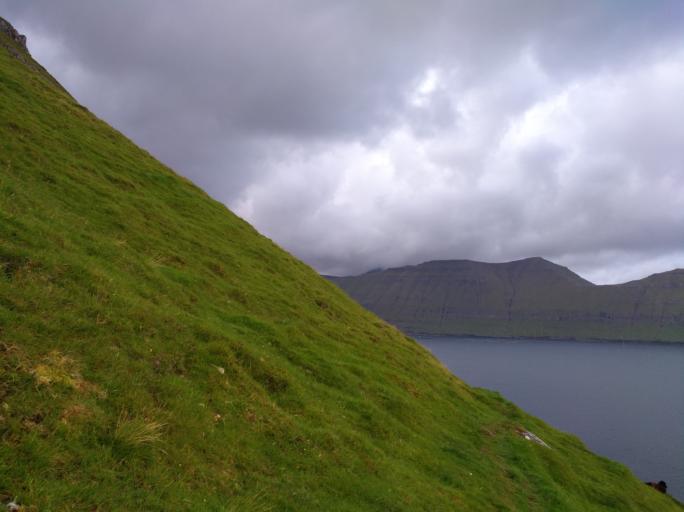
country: FO
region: Eysturoy
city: Fuglafjordur
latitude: 62.2879
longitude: -6.8780
